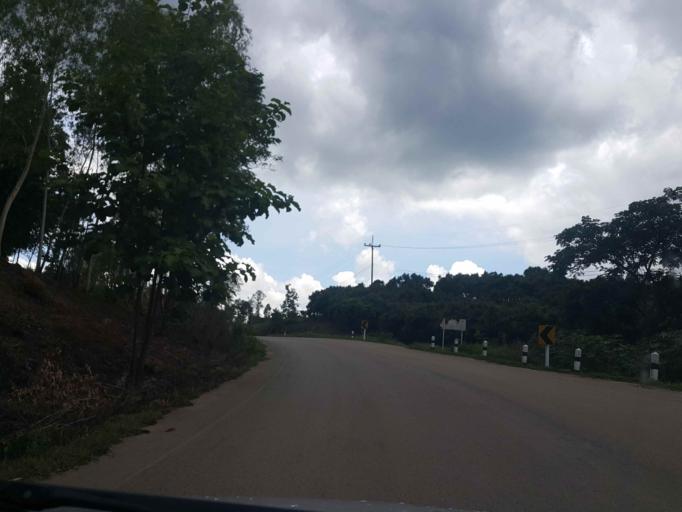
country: TH
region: Phayao
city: Dok Kham Tai
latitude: 18.9630
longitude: 100.0743
